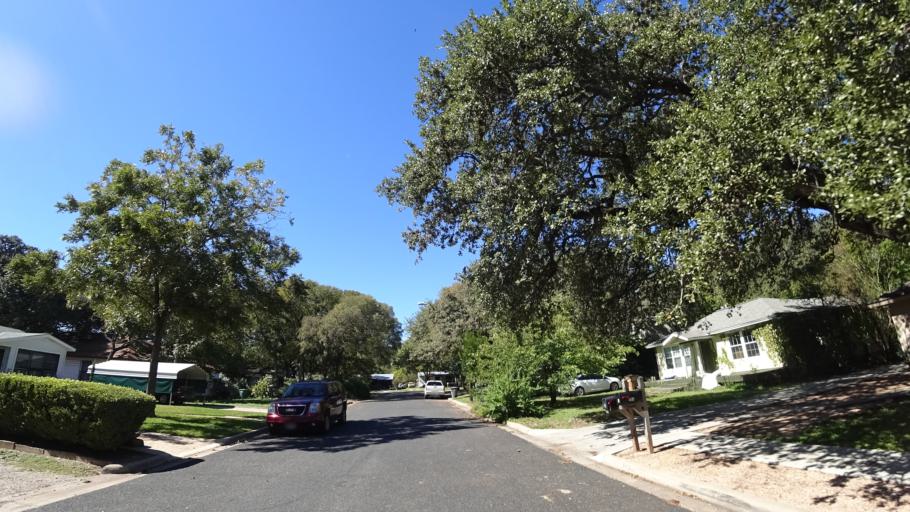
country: US
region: Texas
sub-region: Travis County
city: Rollingwood
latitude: 30.2204
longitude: -97.7787
